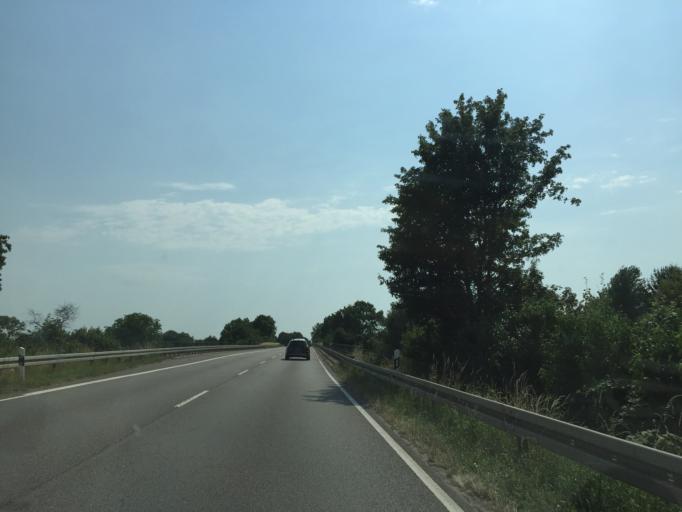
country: DE
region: Baden-Wuerttemberg
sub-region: Karlsruhe Region
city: Weinheim
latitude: 49.5640
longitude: 8.6514
